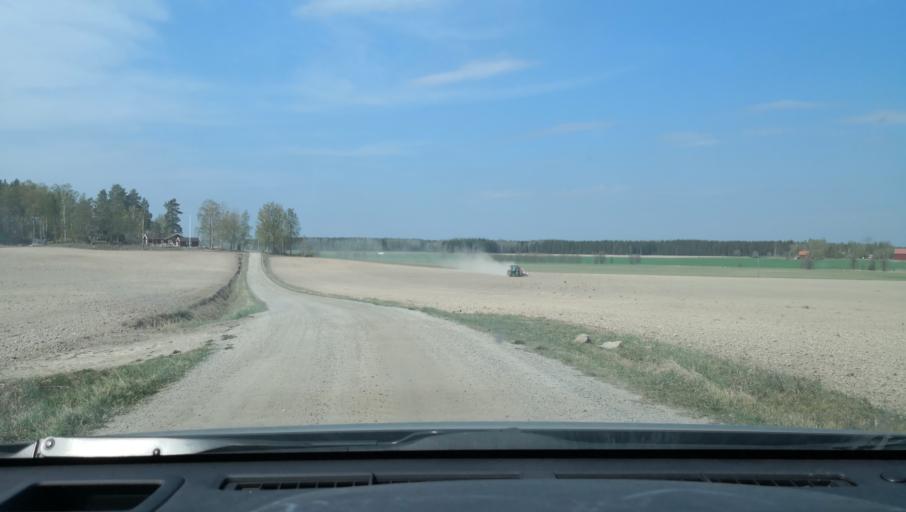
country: SE
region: Vaestmanland
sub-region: Vasteras
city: Skultuna
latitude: 59.7743
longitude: 16.4376
